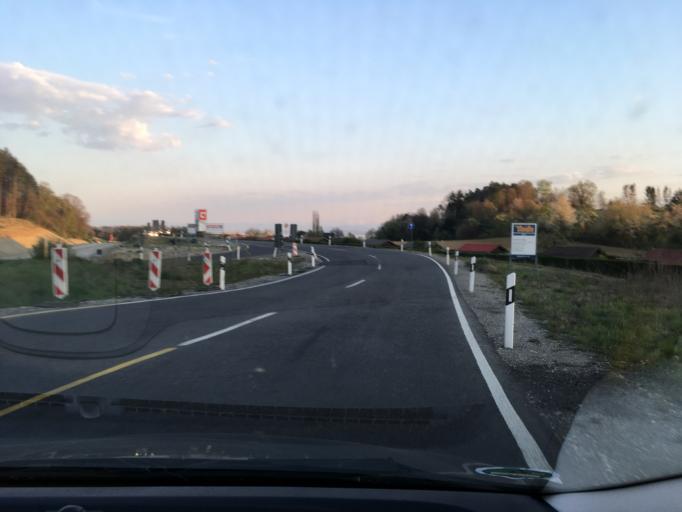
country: DE
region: Baden-Wuerttemberg
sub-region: Tuebingen Region
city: Uberlingen
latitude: 47.7703
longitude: 9.1865
